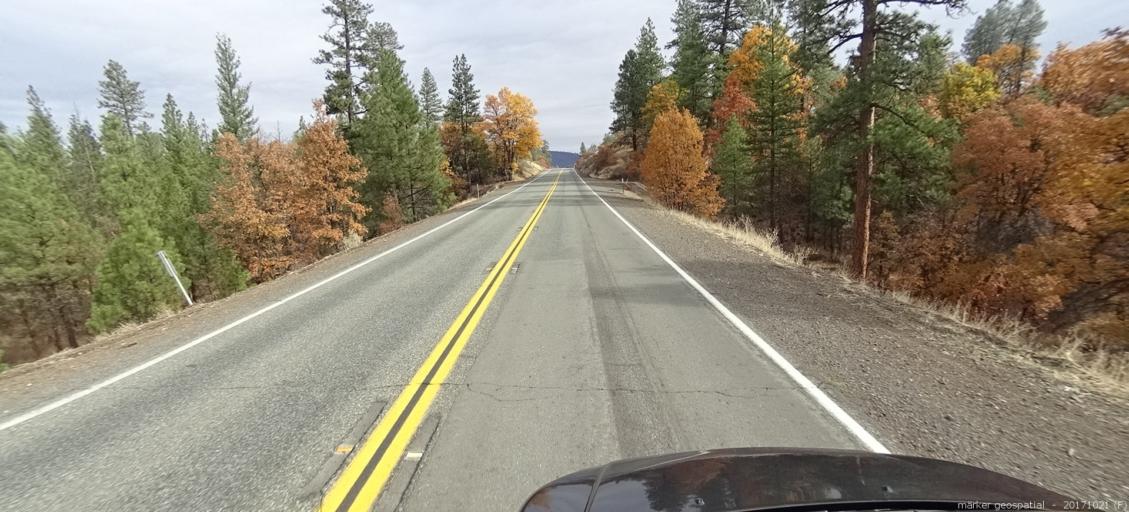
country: US
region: California
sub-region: Shasta County
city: Burney
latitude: 40.9642
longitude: -121.5764
